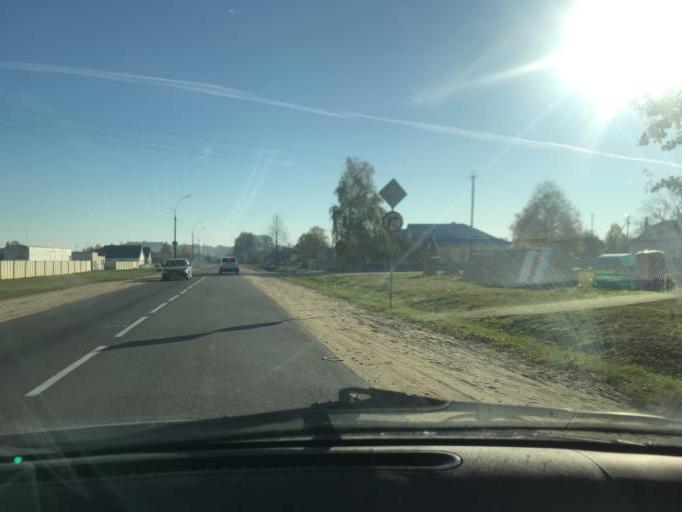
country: BY
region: Brest
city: Ivanava
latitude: 52.1433
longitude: 25.5177
